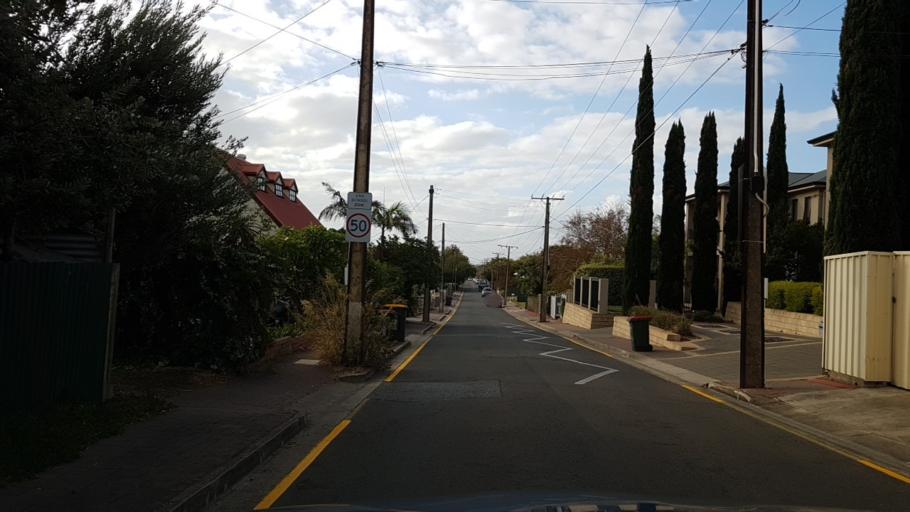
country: AU
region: South Australia
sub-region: Adelaide Hills
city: Seacliff
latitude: -35.0360
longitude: 138.5234
